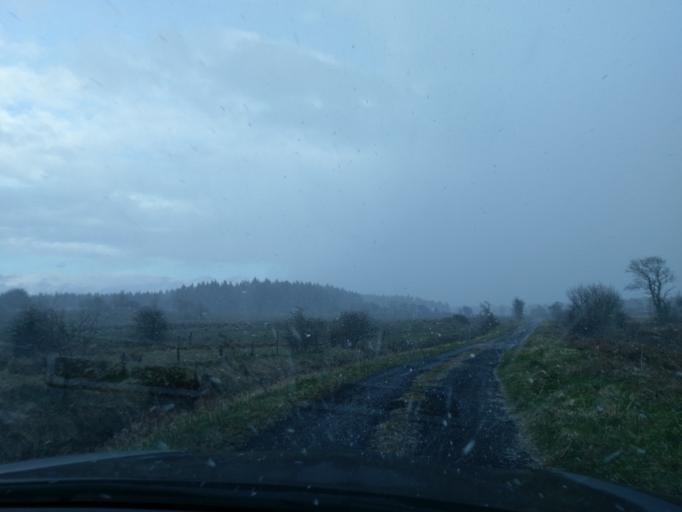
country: IE
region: Connaught
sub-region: County Galway
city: Athenry
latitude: 53.4060
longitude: -8.5960
